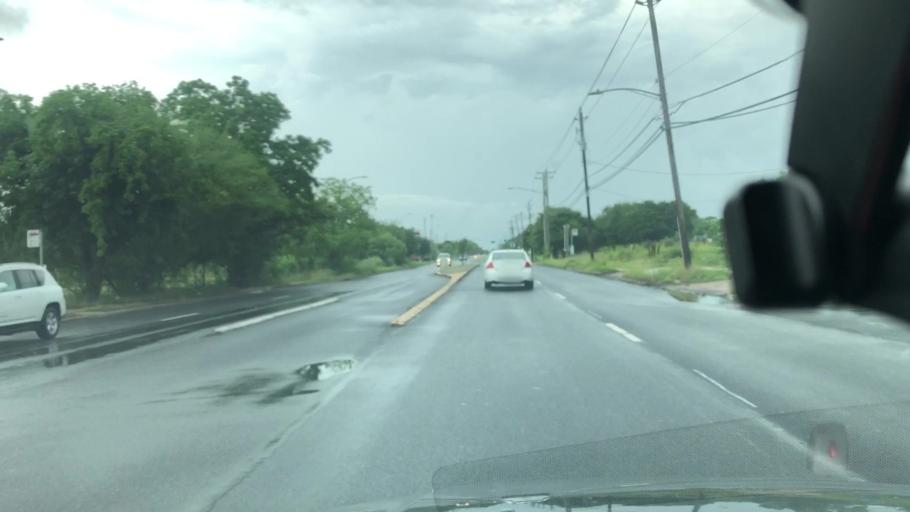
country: US
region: Texas
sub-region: Brazoria County
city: Brookside Village
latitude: 29.6360
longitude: -95.3559
